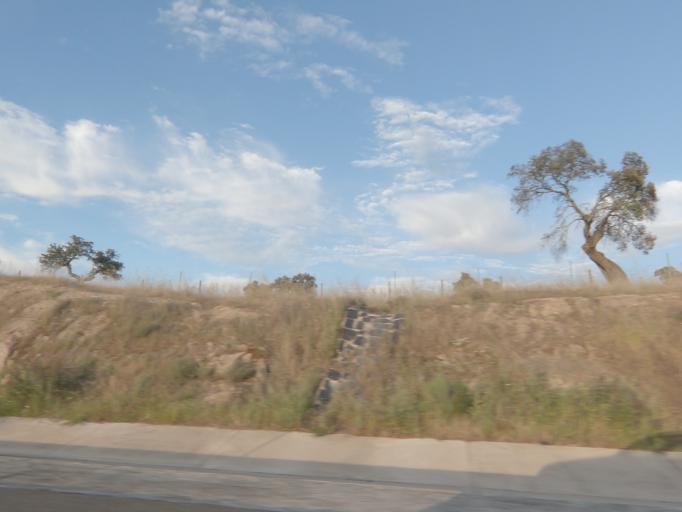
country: ES
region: Extremadura
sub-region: Provincia de Badajoz
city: Aljucen
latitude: 39.0177
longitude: -6.3303
